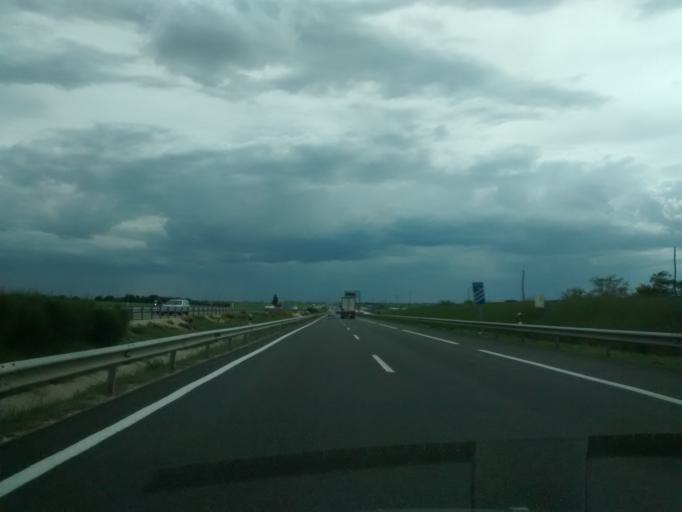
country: ES
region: Castille-La Mancha
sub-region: Provincia de Guadalajara
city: Muduex
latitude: 40.7988
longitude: -2.9578
